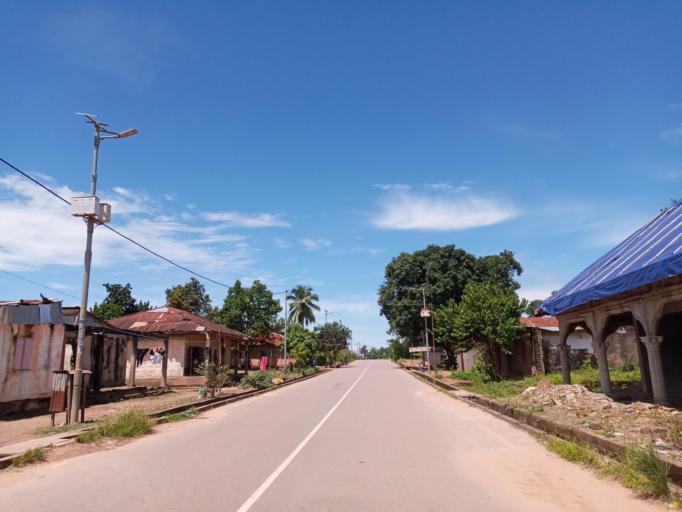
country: SL
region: Eastern Province
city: Koidu
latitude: 8.6469
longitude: -10.9620
